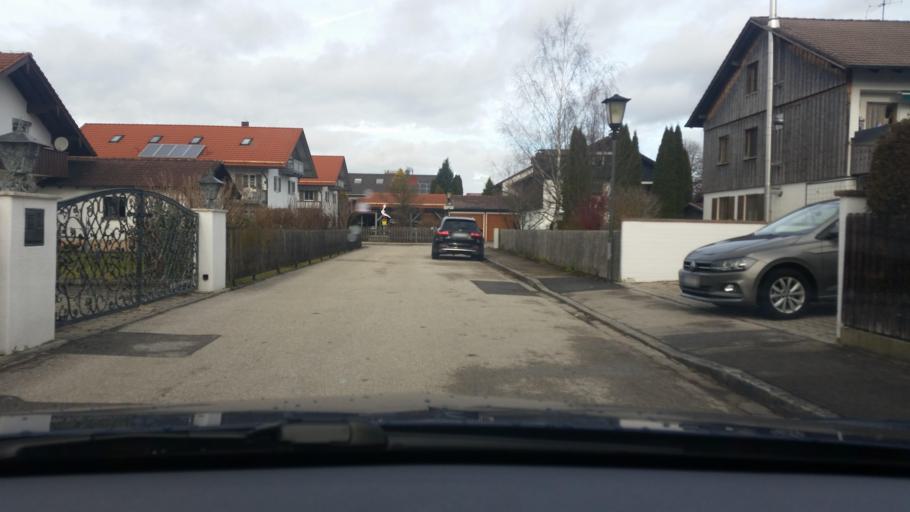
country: DE
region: Bavaria
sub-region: Upper Bavaria
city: Wolfratshausen
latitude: 47.8940
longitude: 11.4260
